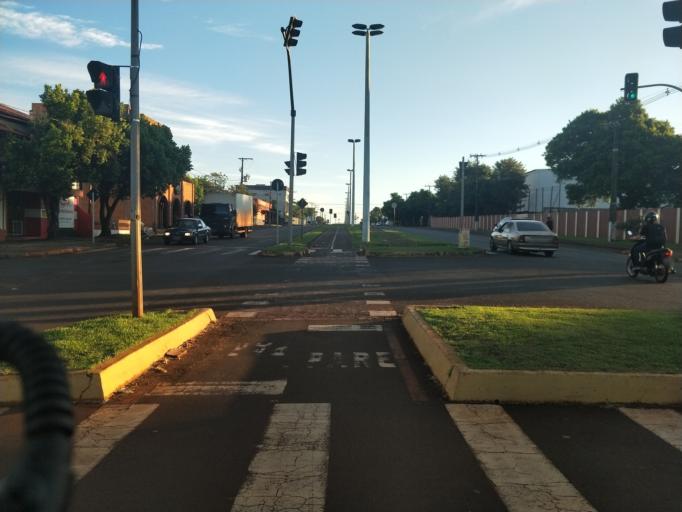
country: BR
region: Parana
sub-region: Marechal Candido Rondon
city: Marechal Candido Rondon
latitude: -24.5580
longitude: -54.0483
